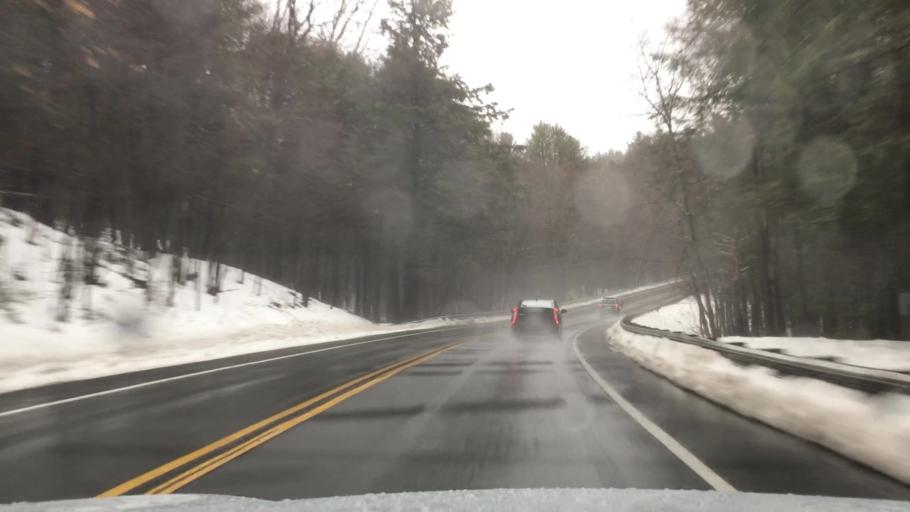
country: US
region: Massachusetts
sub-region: Franklin County
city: Shutesbury
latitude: 42.4280
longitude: -72.3986
